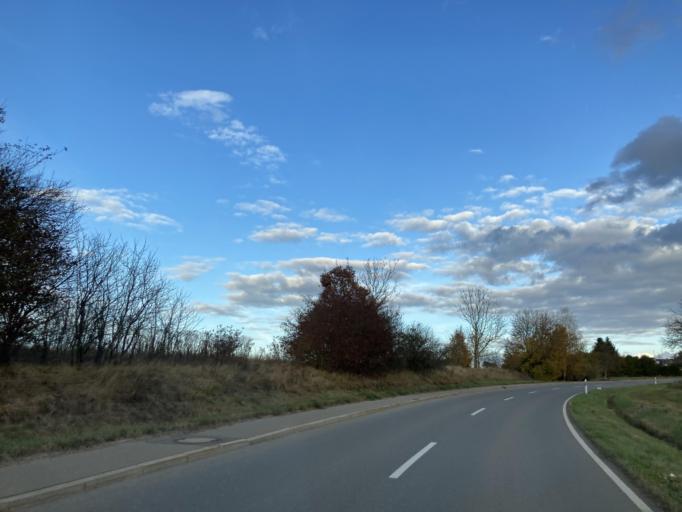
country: DE
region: Baden-Wuerttemberg
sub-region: Tuebingen Region
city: Gomaringen
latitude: 48.4746
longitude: 9.1275
